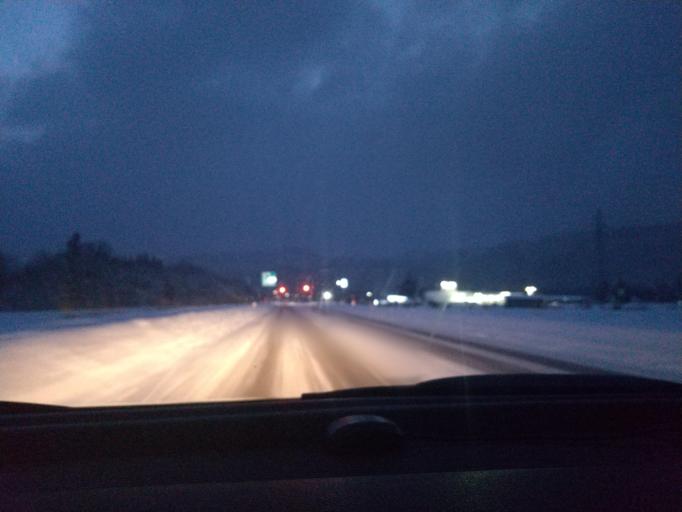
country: JP
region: Akita
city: Kakunodatemachi
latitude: 39.6937
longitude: 140.7238
